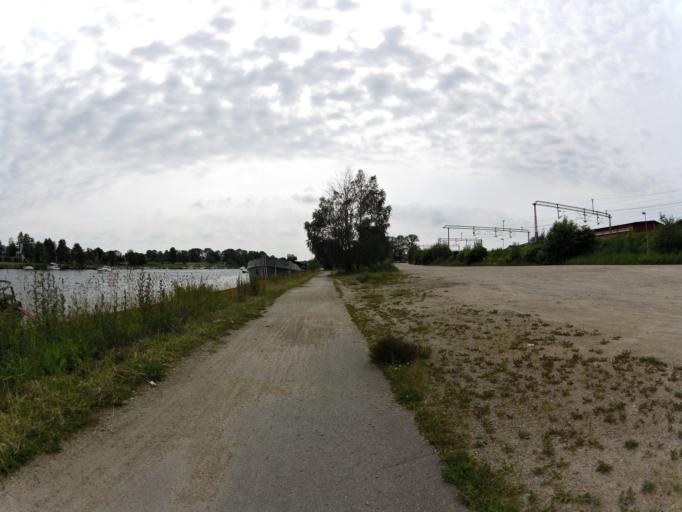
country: NO
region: Ostfold
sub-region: Fredrikstad
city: Fredrikstad
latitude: 59.2106
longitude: 10.9590
